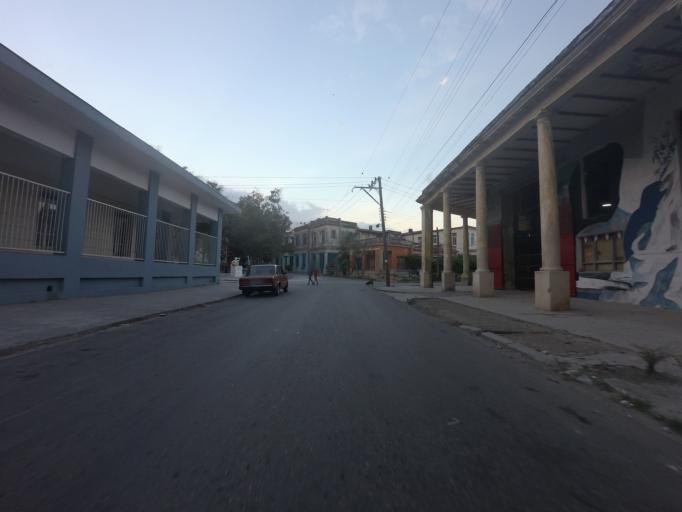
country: CU
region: La Habana
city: Havana
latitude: 23.1295
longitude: -82.3789
